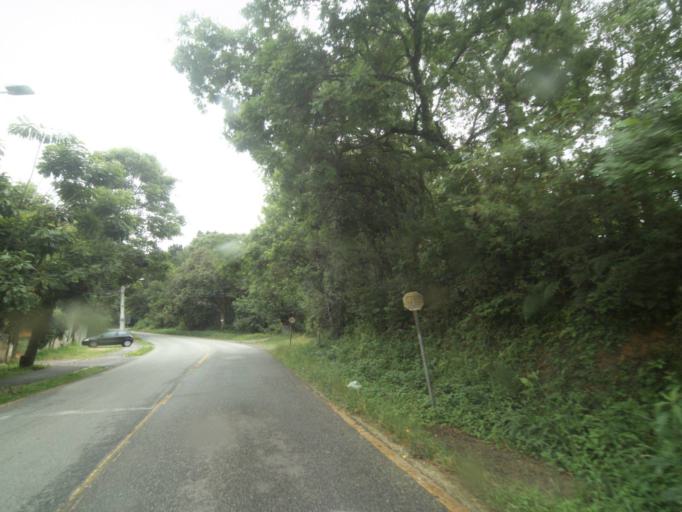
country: BR
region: Parana
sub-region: Curitiba
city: Curitiba
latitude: -25.4269
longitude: -49.3332
